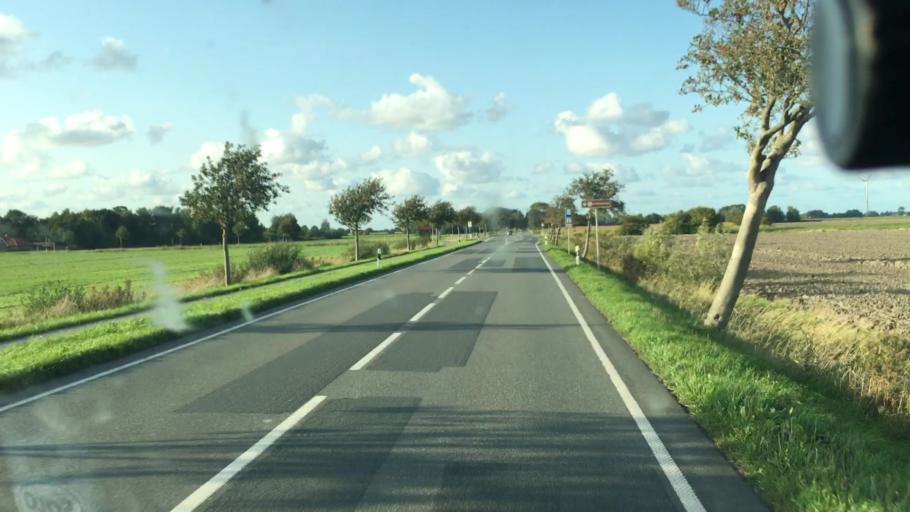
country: DE
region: Lower Saxony
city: Werdum
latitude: 53.6499
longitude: 7.7900
